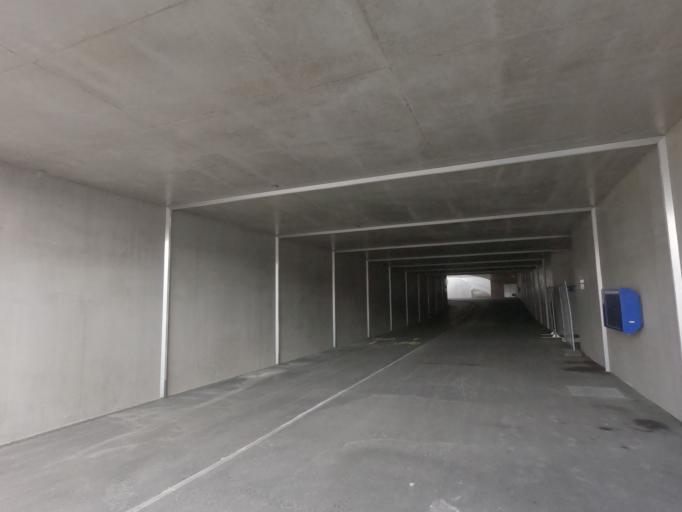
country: CH
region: Vaud
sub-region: Ouest Lausannois District
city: Prilly
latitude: 46.5272
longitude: 6.6007
